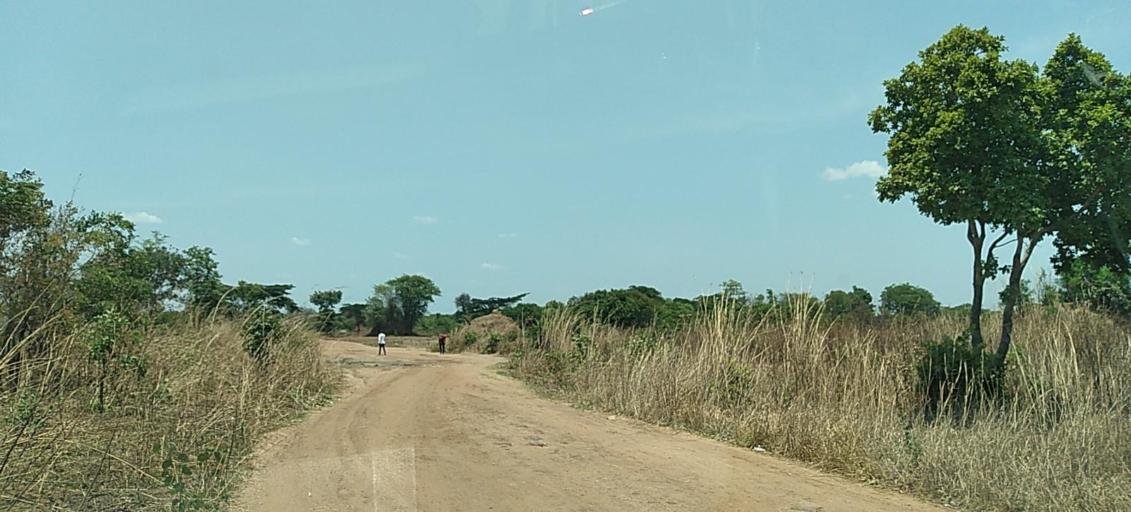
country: ZM
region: Copperbelt
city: Luanshya
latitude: -13.0959
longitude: 28.4061
